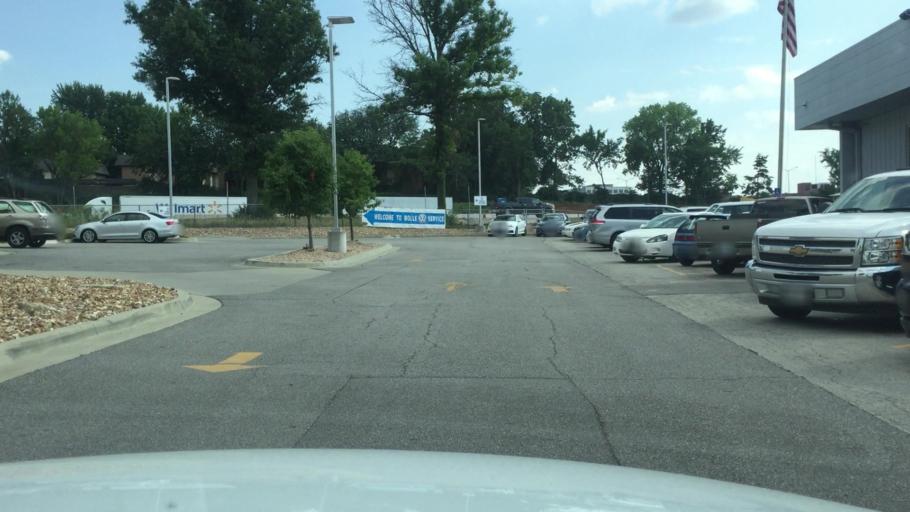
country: US
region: Kansas
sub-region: Johnson County
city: Leawood
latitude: 38.9402
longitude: -94.6013
